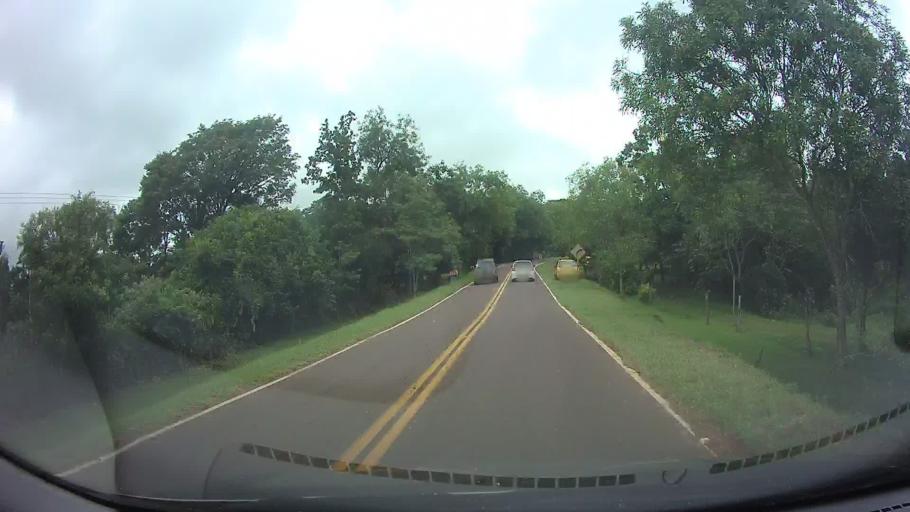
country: PY
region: Paraguari
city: Acahay
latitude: -25.9276
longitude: -57.1076
